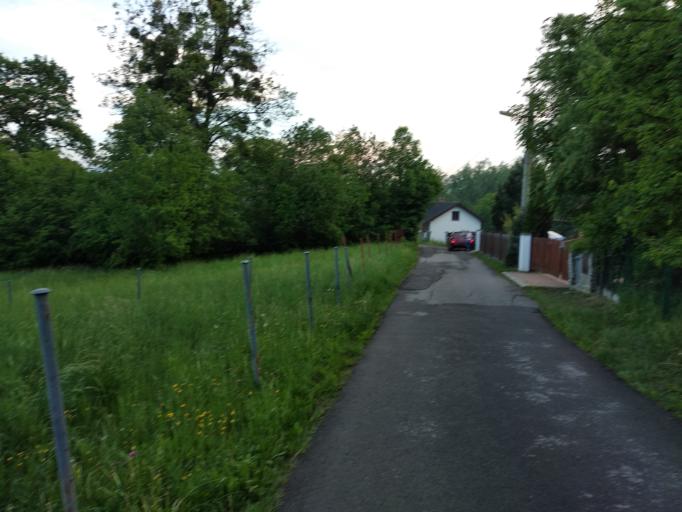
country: CZ
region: Moravskoslezsky
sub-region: Okres Frydek-Mistek
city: Stare Mesto
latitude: 49.6916
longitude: 18.3720
